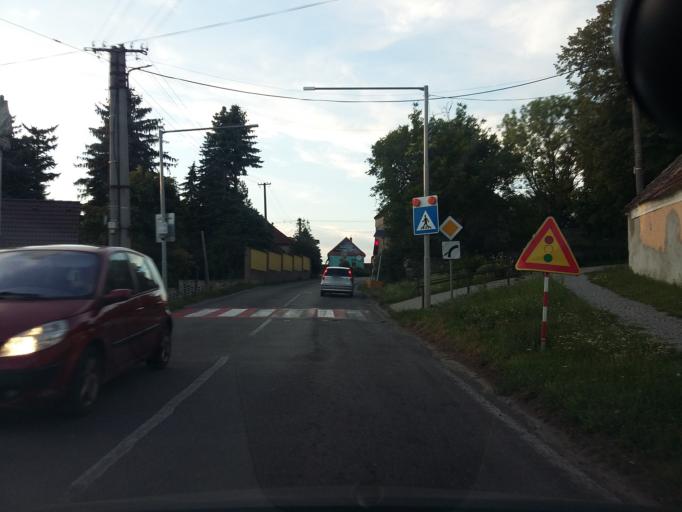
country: SK
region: Bratislavsky
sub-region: Okres Malacky
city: Malacky
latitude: 48.4058
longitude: 17.1548
